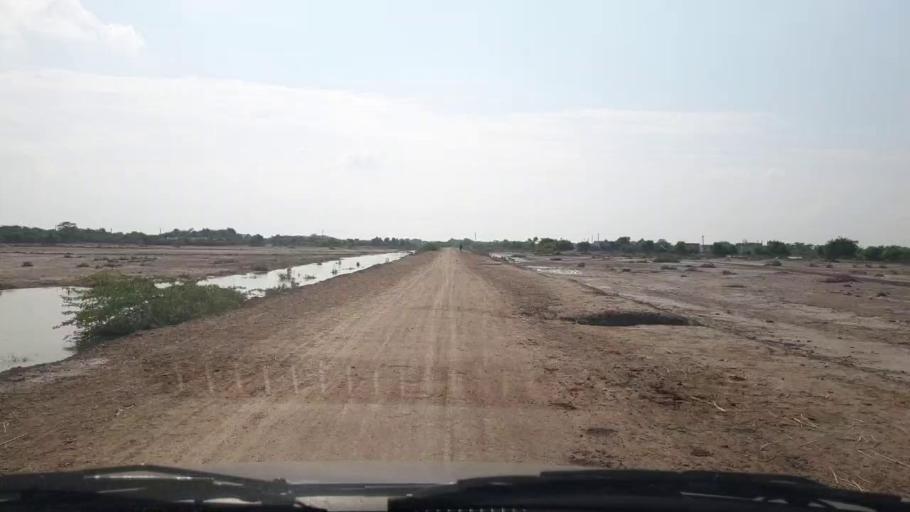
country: PK
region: Sindh
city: Badin
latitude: 24.4824
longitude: 68.6124
